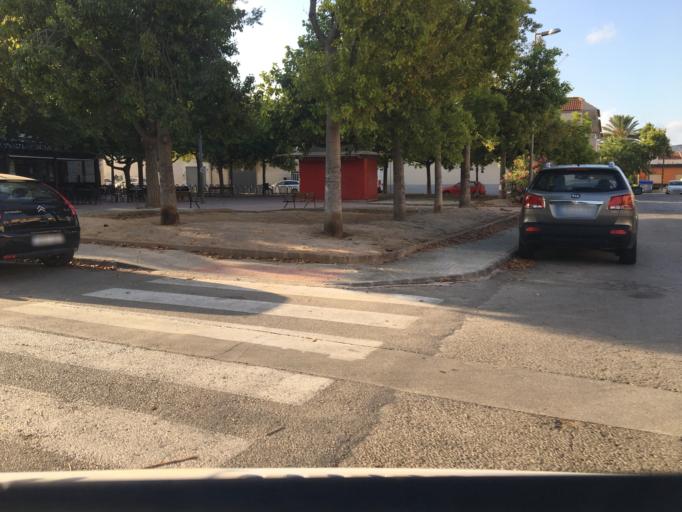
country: ES
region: Murcia
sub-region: Murcia
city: Cartagena
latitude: 37.6189
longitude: -1.0013
